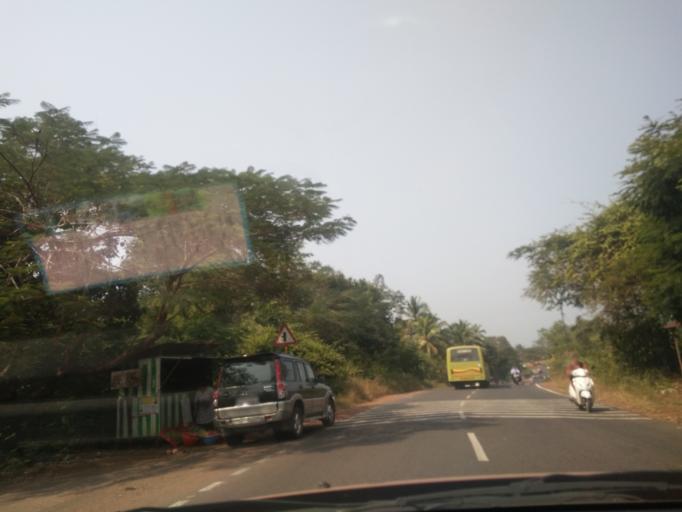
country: IN
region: Goa
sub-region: North Goa
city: Aldona
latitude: 15.6232
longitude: 73.8825
